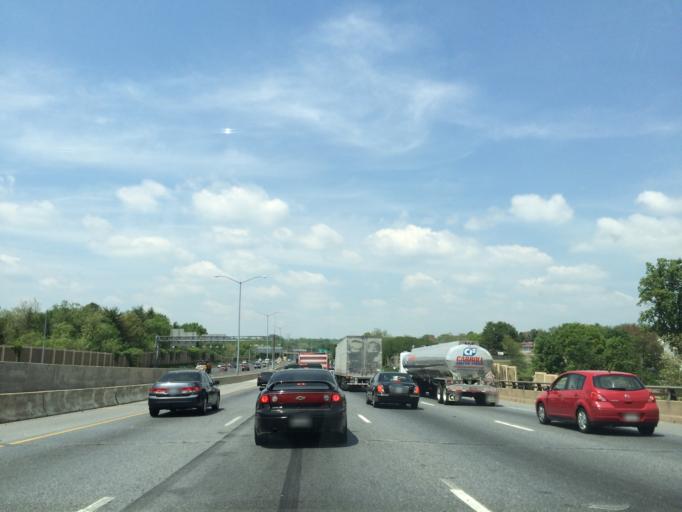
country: US
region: Maryland
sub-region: Baltimore County
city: Arbutus
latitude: 39.2563
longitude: -76.6915
